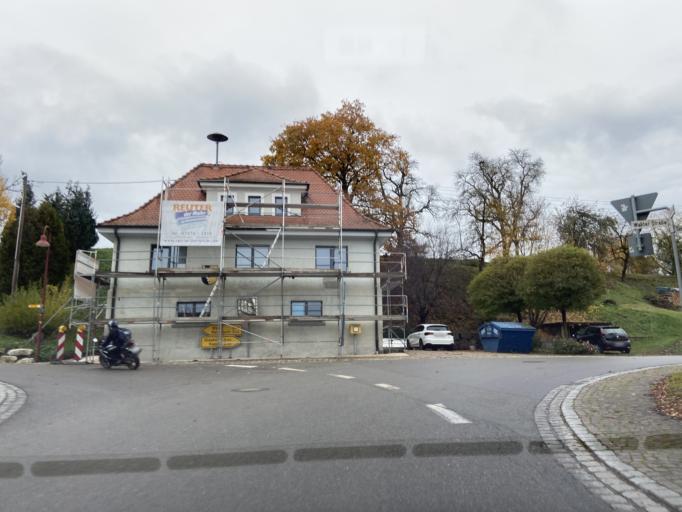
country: DE
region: Baden-Wuerttemberg
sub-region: Tuebingen Region
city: Pfullendorf
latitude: 47.9584
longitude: 9.2268
